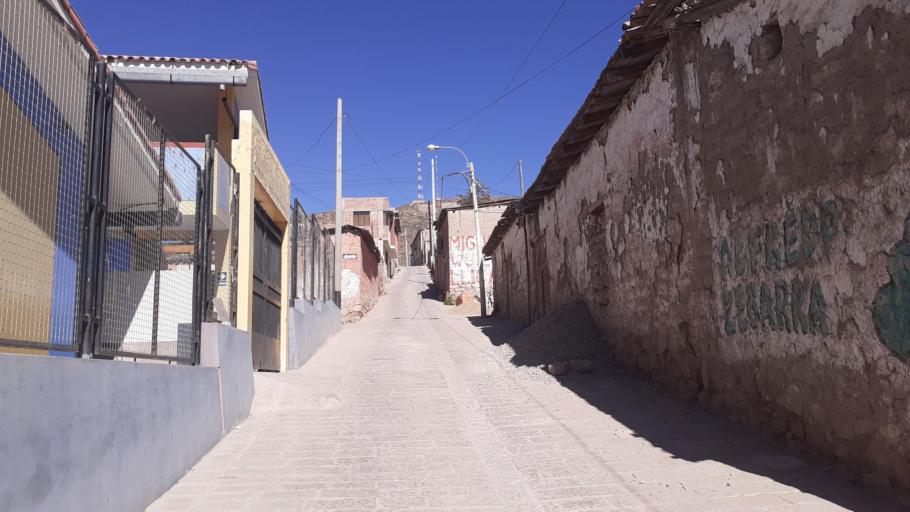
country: PE
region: Arequipa
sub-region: Provincia de Condesuyos
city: Chuquibamba
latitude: -15.8367
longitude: -72.6553
